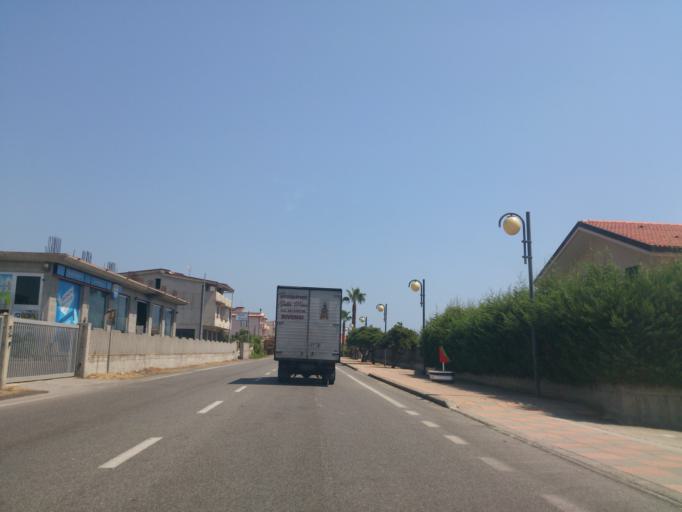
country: IT
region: Calabria
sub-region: Provincia di Reggio Calabria
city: Riace Marina
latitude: 38.3942
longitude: 16.5346
